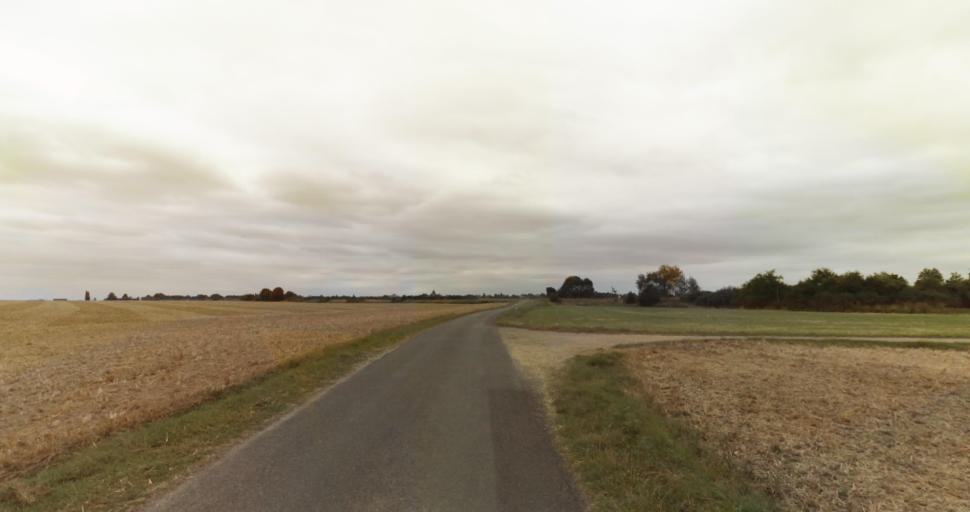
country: FR
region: Haute-Normandie
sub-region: Departement de l'Eure
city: Evreux
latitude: 48.9730
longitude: 1.2238
